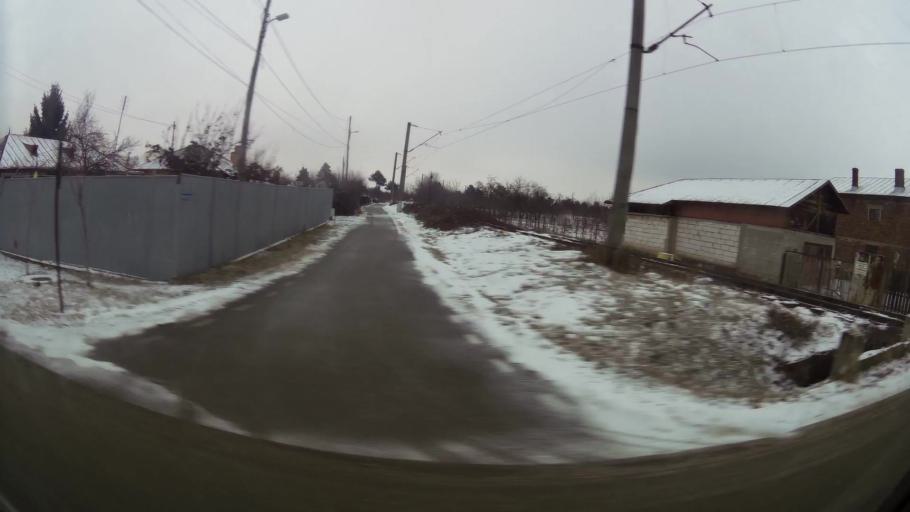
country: RO
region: Prahova
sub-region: Comuna Berceni
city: Corlatesti
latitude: 44.9176
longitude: 26.0826
